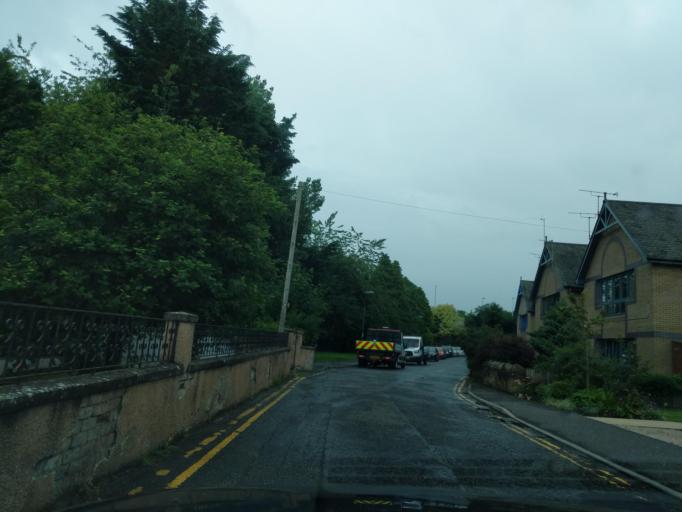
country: GB
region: Scotland
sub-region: Midlothian
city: Dalkeith
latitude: 55.8958
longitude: -3.0756
